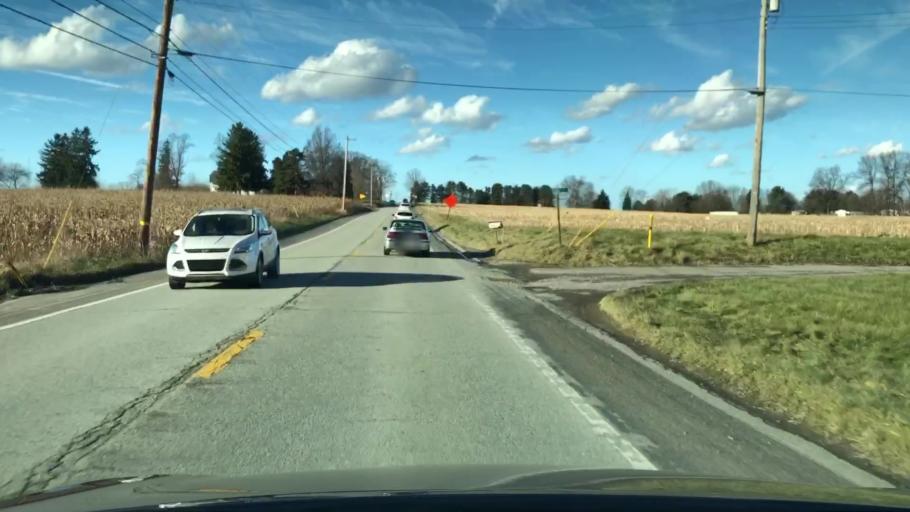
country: US
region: Pennsylvania
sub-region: Butler County
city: Saxonburg
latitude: 40.7533
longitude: -79.7745
